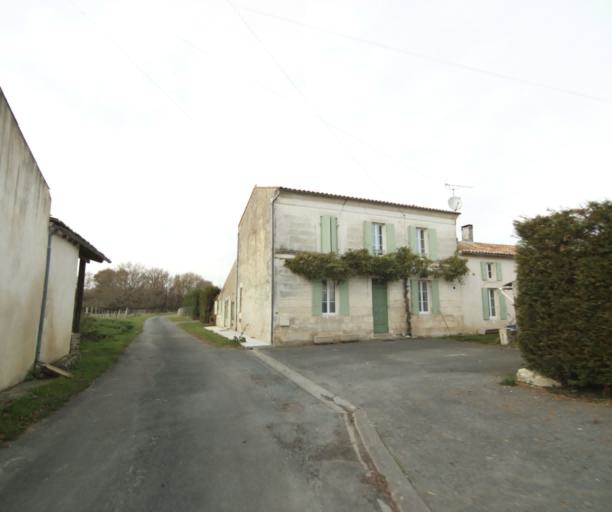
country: FR
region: Poitou-Charentes
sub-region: Departement de la Charente-Maritime
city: Fontcouverte
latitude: 45.7910
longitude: -0.5972
